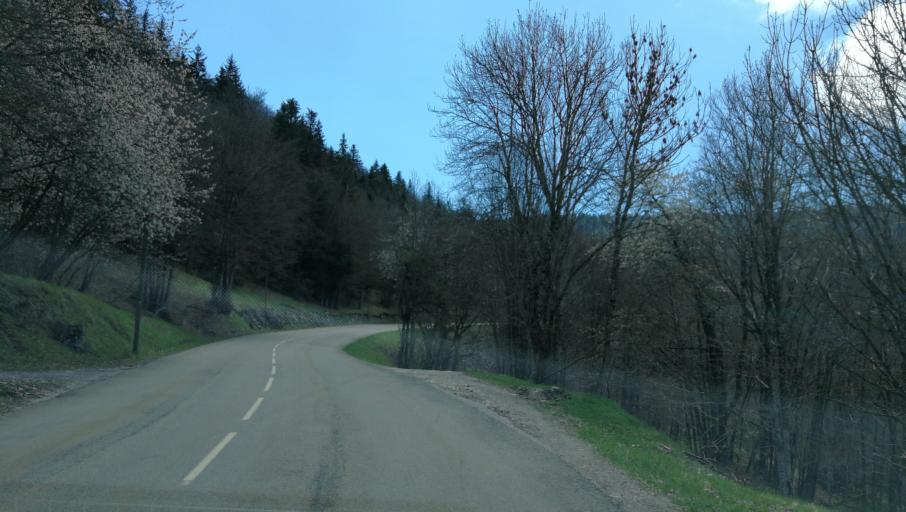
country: FR
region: Rhone-Alpes
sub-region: Departement de la Drome
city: Die
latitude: 44.8789
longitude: 5.3984
